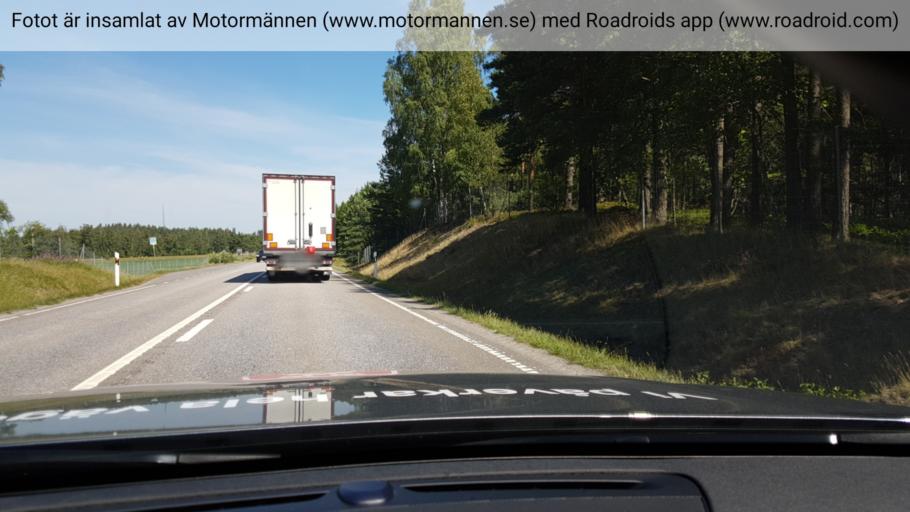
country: SE
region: OErebro
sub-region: Hallsbergs Kommun
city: Palsboda
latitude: 58.9965
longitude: 15.4049
